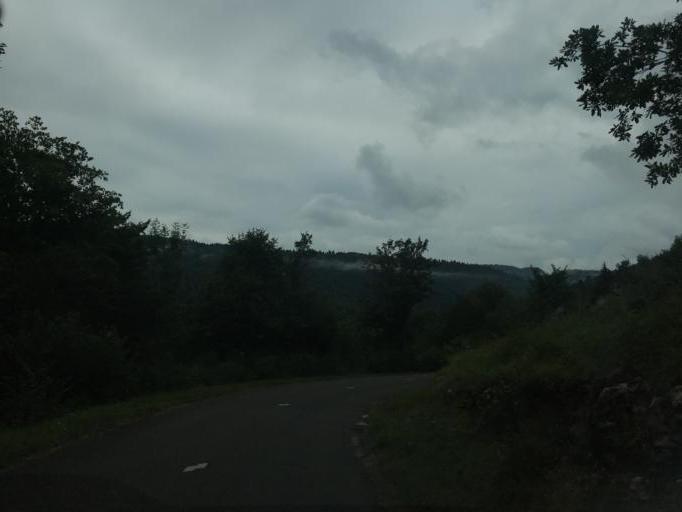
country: FR
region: Franche-Comte
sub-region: Departement du Jura
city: Lavans-les-Saint-Claude
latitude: 46.3223
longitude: 5.7536
